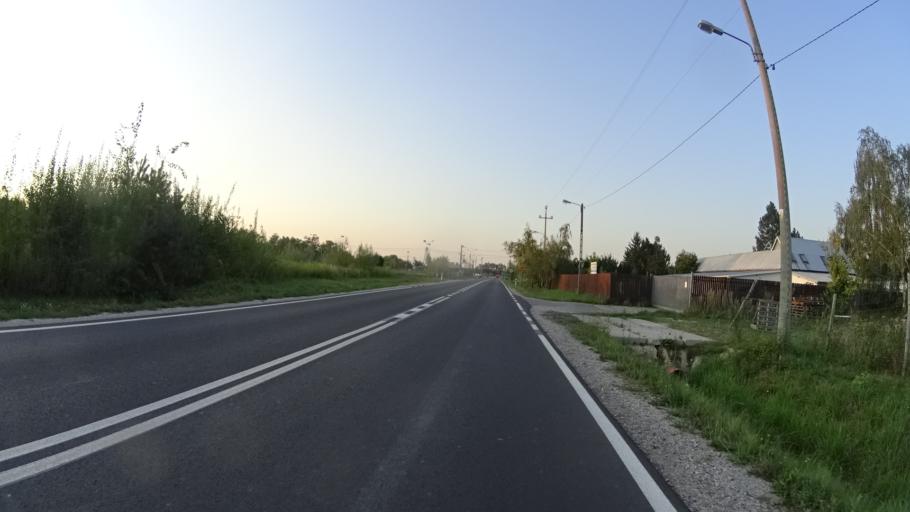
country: PL
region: Masovian Voivodeship
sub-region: Powiat warszawski zachodni
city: Truskaw
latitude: 52.2507
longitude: 20.7413
